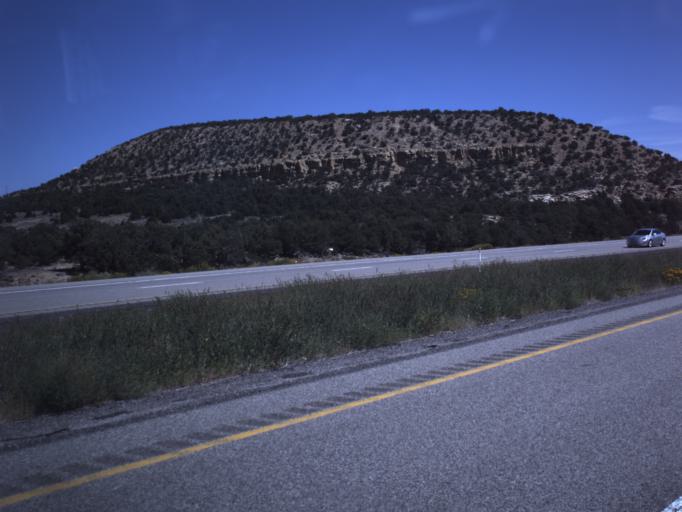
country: US
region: Utah
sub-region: Wayne County
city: Loa
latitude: 38.7579
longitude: -111.4099
